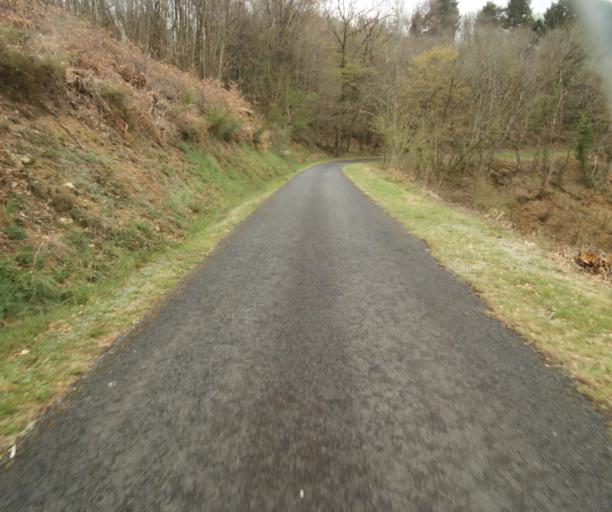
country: FR
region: Limousin
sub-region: Departement de la Correze
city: Naves
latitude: 45.2997
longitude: 1.8107
